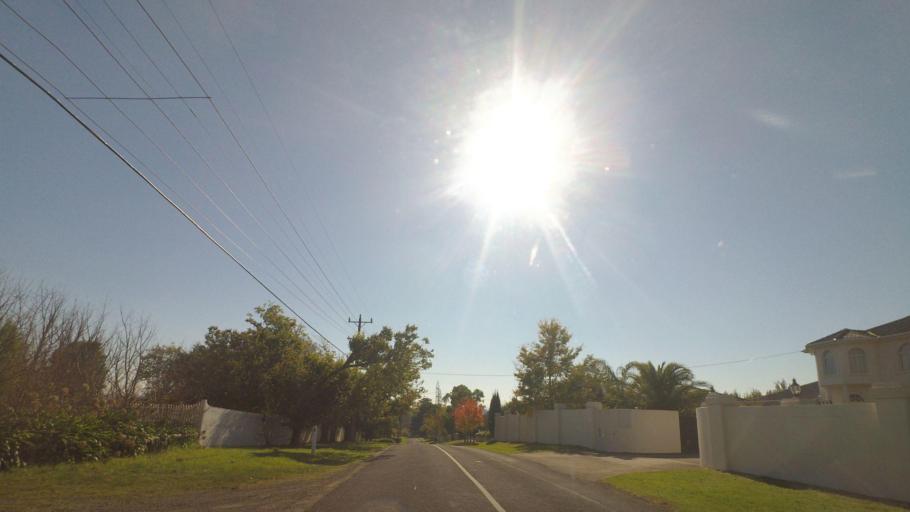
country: AU
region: Victoria
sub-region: Nillumbik
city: Eltham
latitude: -37.7473
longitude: 145.1585
